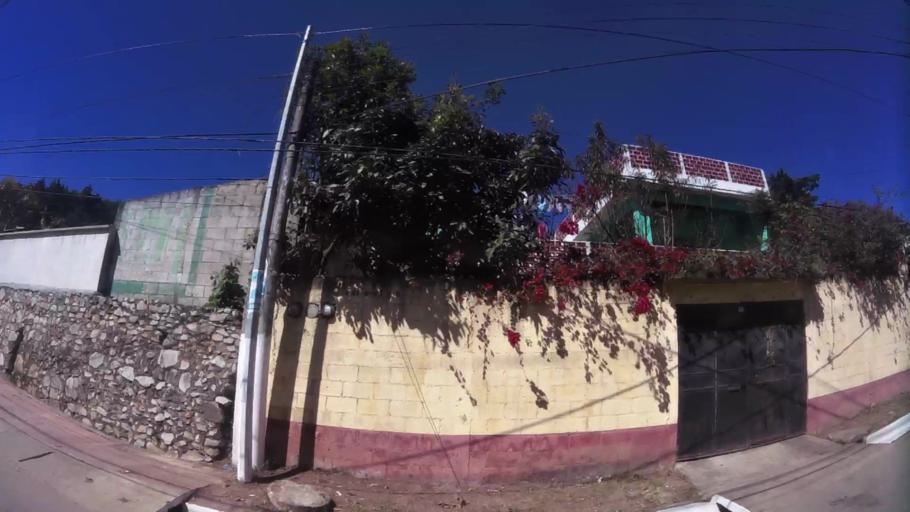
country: GT
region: Guatemala
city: San Jose Pinula
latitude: 14.5203
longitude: -90.4230
